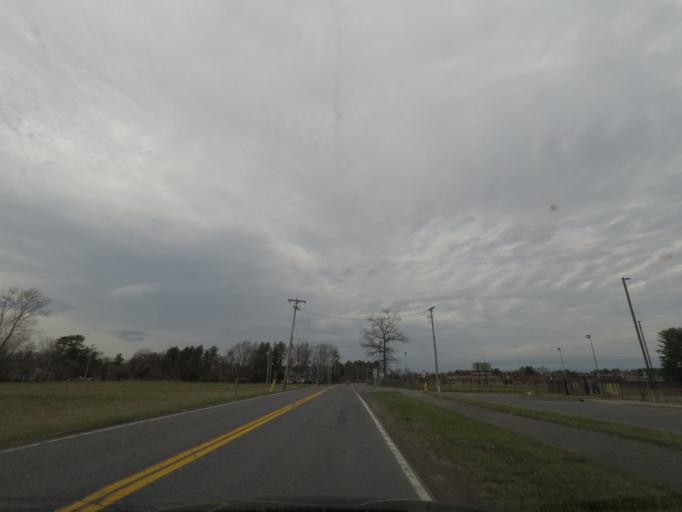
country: US
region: New York
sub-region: Albany County
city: Delmar
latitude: 42.6076
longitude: -73.8564
